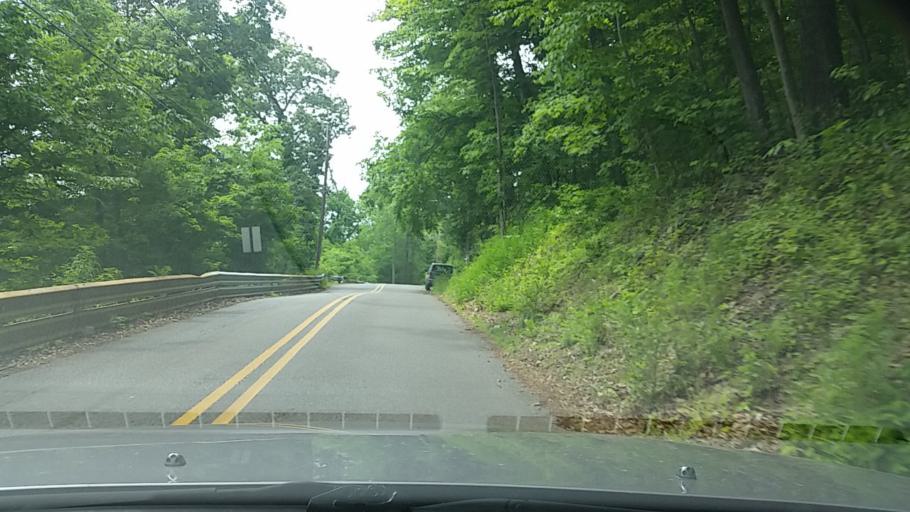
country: US
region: New Jersey
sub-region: Warren County
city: Oxford
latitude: 40.8630
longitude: -74.9848
